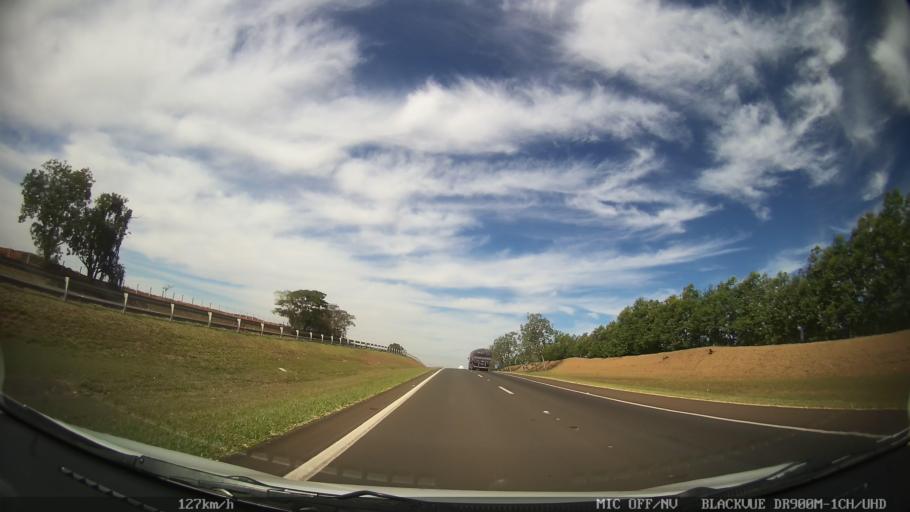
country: BR
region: Sao Paulo
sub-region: Matao
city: Matao
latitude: -21.6089
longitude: -48.4251
